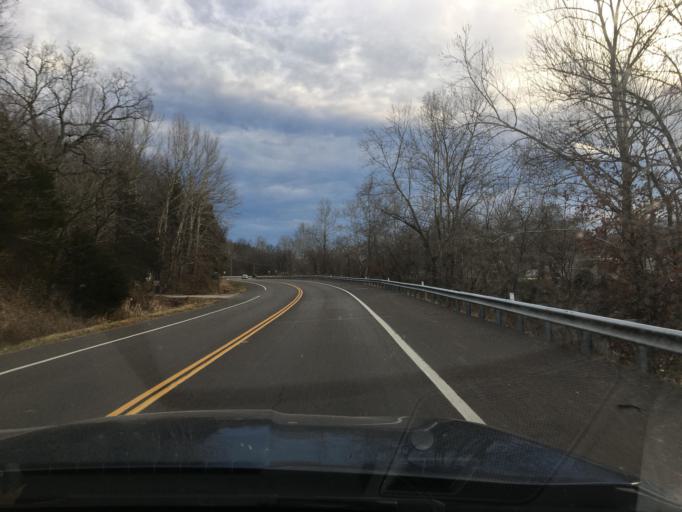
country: US
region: Missouri
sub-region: Jefferson County
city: De Soto
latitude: 38.1306
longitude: -90.5547
